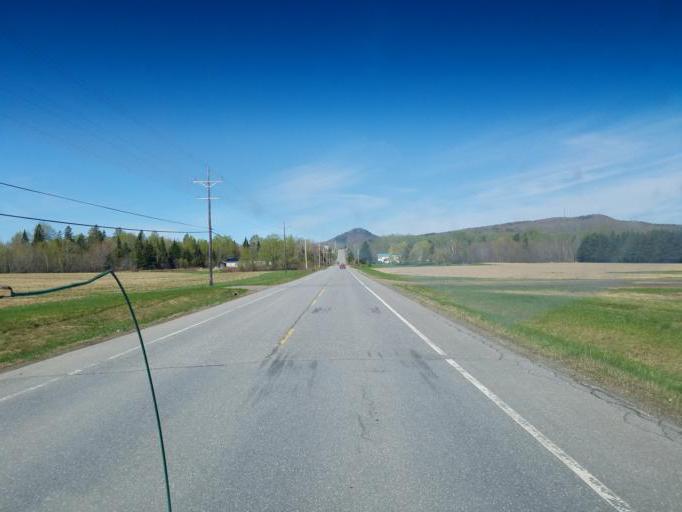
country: US
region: Maine
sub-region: Aroostook County
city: Presque Isle
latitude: 46.6670
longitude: -68.1988
